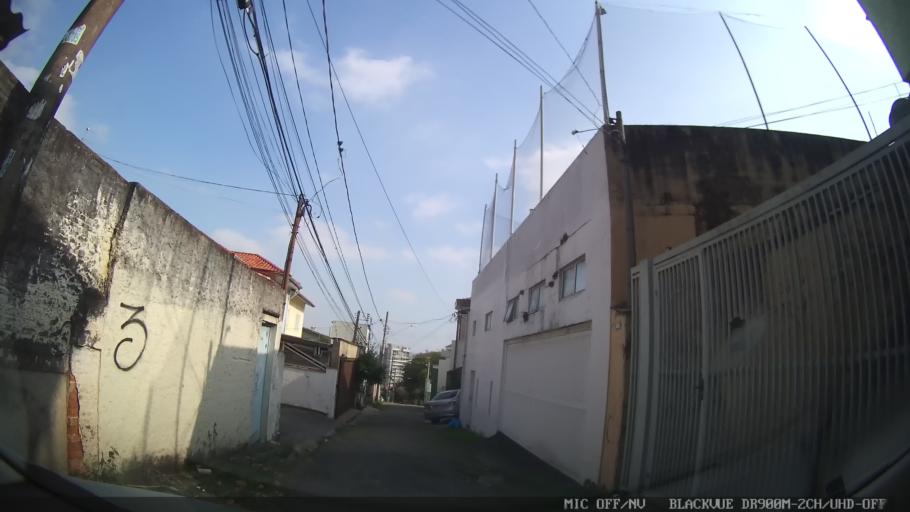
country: BR
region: Sao Paulo
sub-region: Sao Paulo
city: Sao Paulo
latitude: -23.4972
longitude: -46.6186
